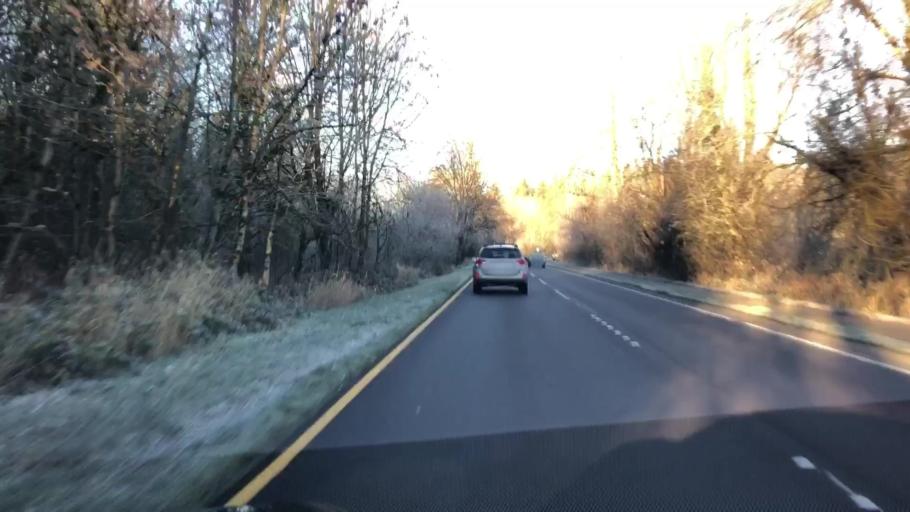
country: US
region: Washington
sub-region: King County
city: Bellevue
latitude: 47.6014
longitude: -122.1719
